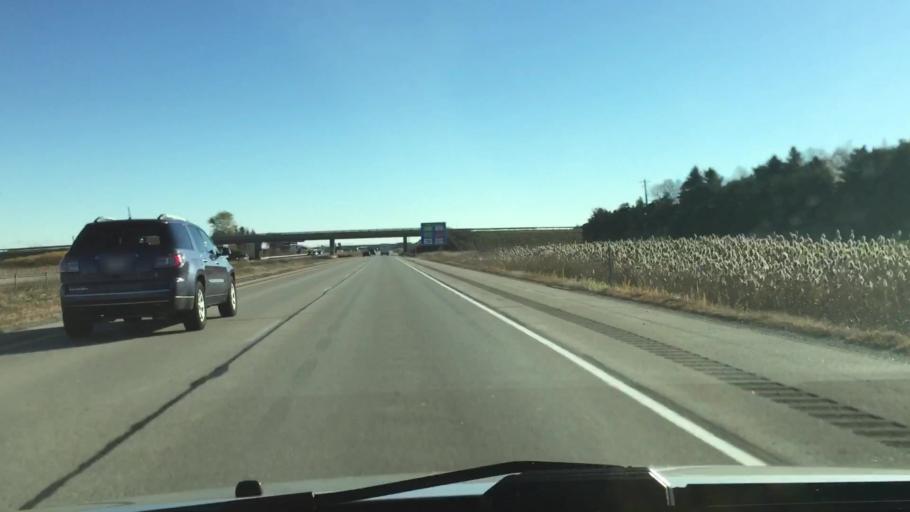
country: US
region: Wisconsin
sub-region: Outagamie County
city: Little Chute
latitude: 44.2978
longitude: -88.3363
